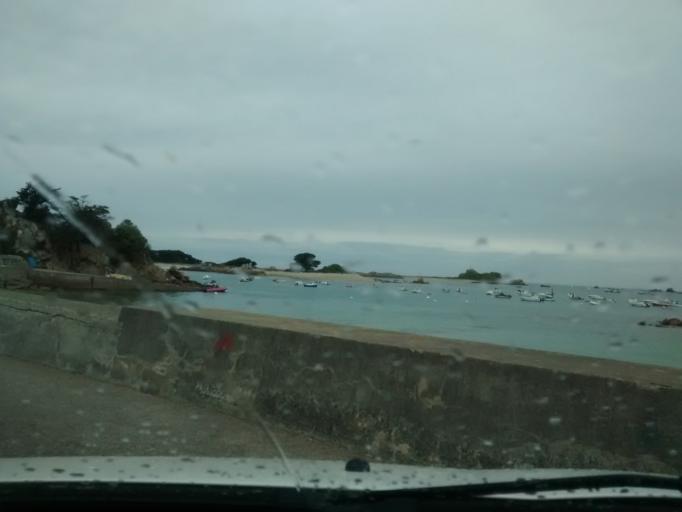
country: FR
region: Brittany
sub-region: Departement des Cotes-d'Armor
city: Trevou-Treguignec
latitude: 48.8375
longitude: -3.3186
